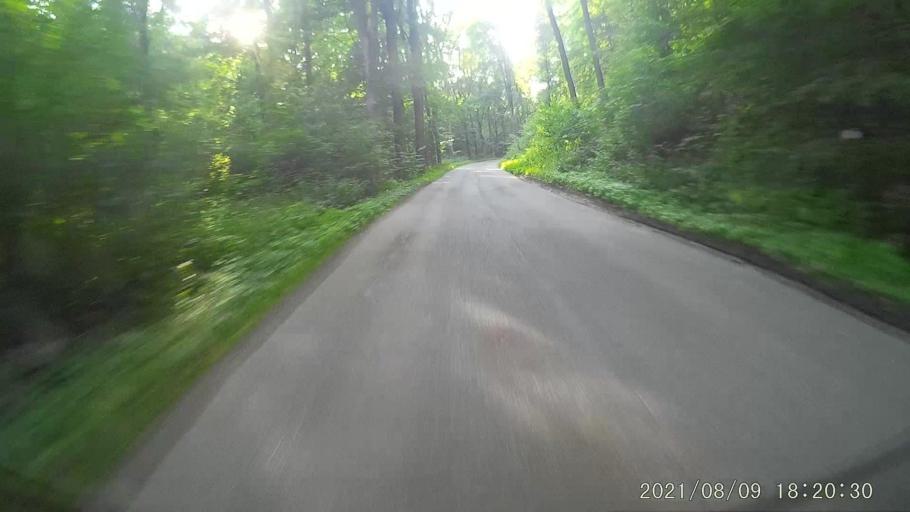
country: PL
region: Lower Silesian Voivodeship
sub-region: Powiat zabkowicki
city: Bardo
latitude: 50.5127
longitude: 16.6883
